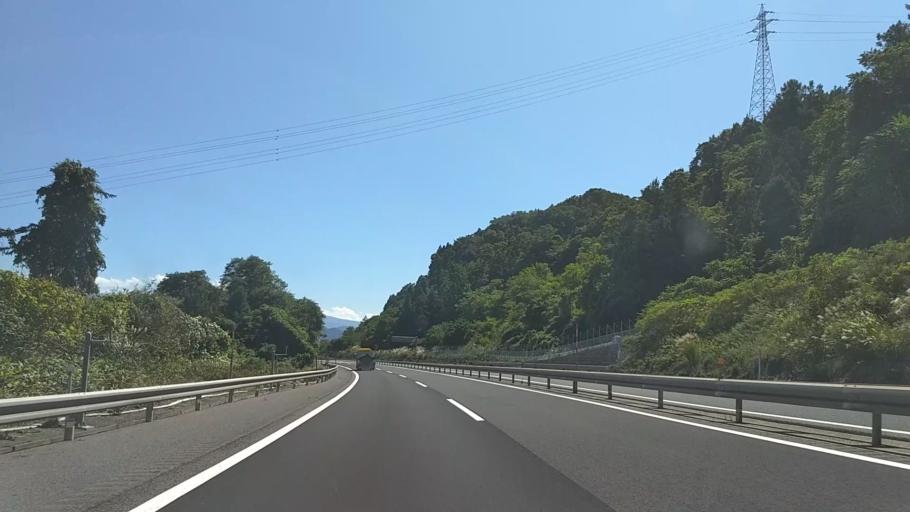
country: JP
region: Nagano
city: Nakano
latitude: 36.7804
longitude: 138.3172
